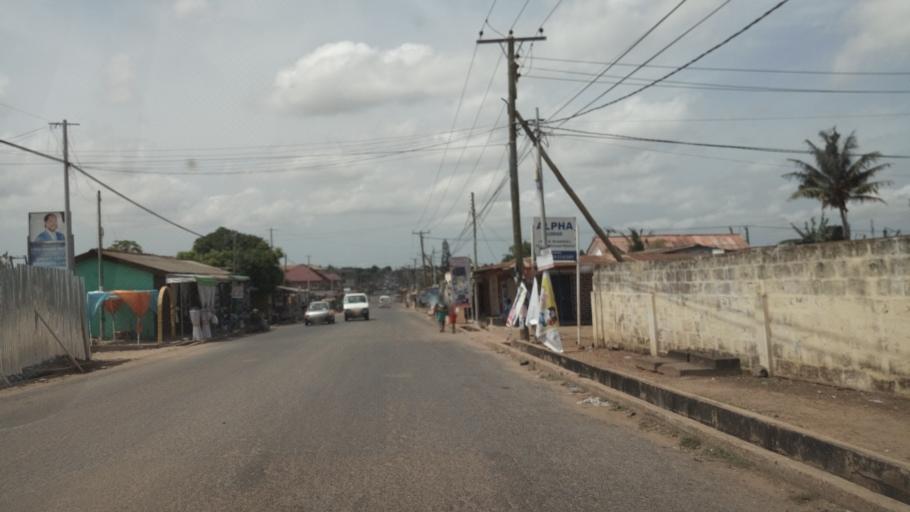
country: GH
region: Greater Accra
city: Medina Estates
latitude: 5.6846
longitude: -0.1605
